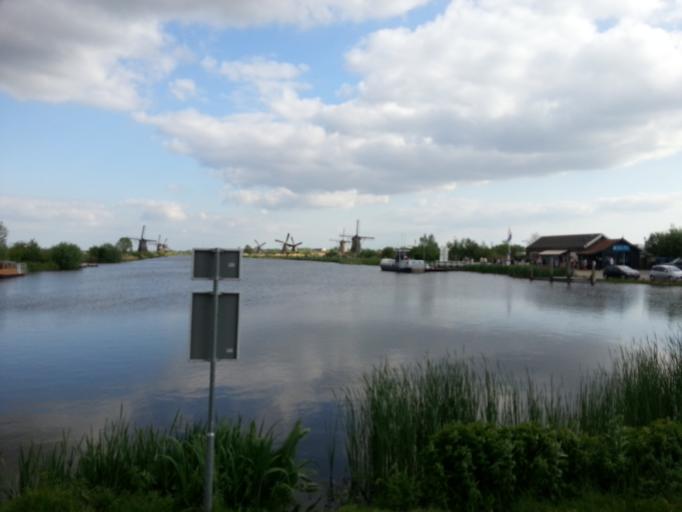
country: NL
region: South Holland
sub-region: Gemeente Alblasserdam
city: Alblasserdam
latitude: 51.8885
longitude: 4.6380
